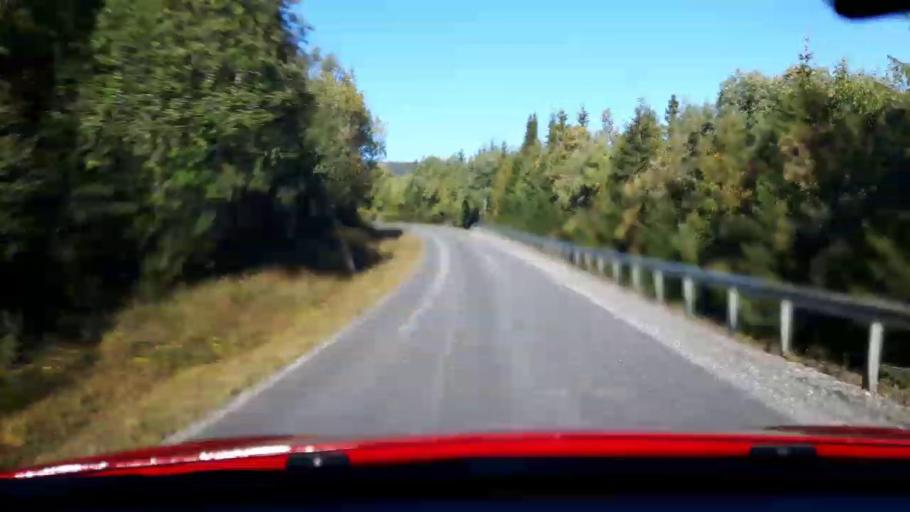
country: NO
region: Nord-Trondelag
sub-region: Lierne
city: Sandvika
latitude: 64.5849
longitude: 13.8847
